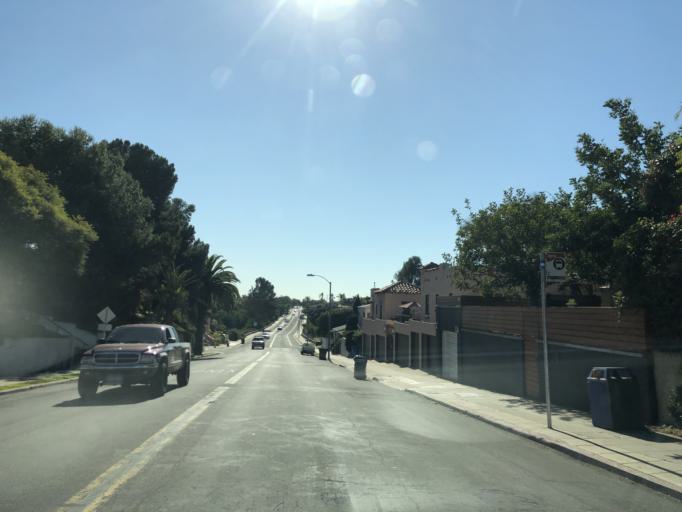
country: US
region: California
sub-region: San Diego County
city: San Diego
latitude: 32.7356
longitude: -117.1293
